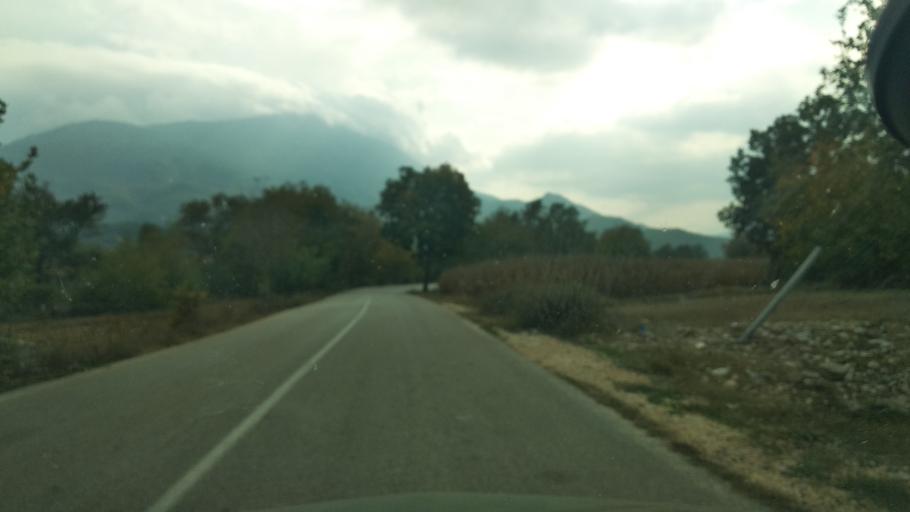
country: GR
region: Thessaly
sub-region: Trikala
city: Kastraki
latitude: 39.7049
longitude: 21.5265
